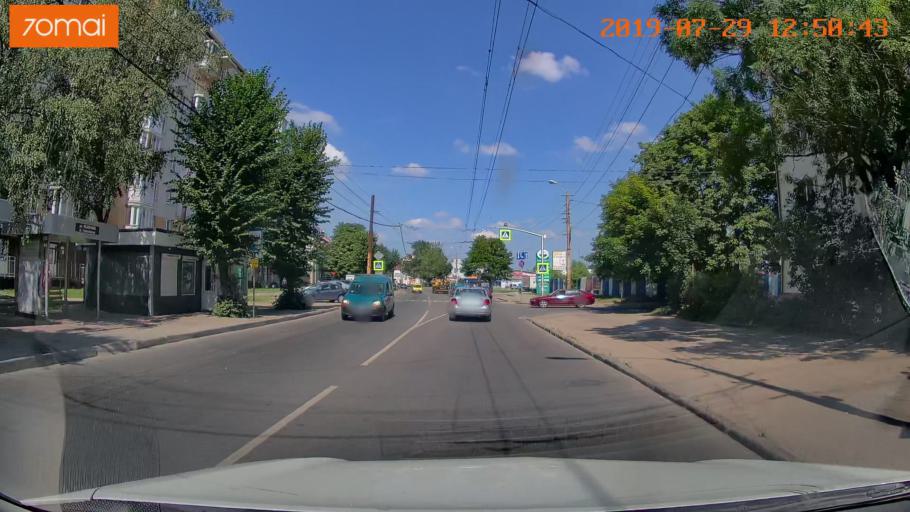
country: RU
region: Kaliningrad
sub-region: Gorod Kaliningrad
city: Kaliningrad
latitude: 54.6888
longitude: 20.5322
